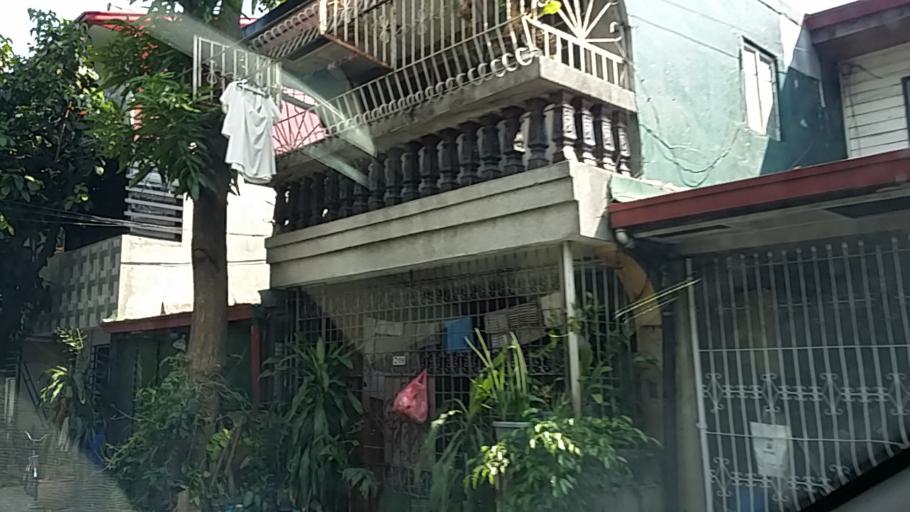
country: PH
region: Metro Manila
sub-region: Mandaluyong
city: Mandaluyong City
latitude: 14.5727
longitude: 121.0369
